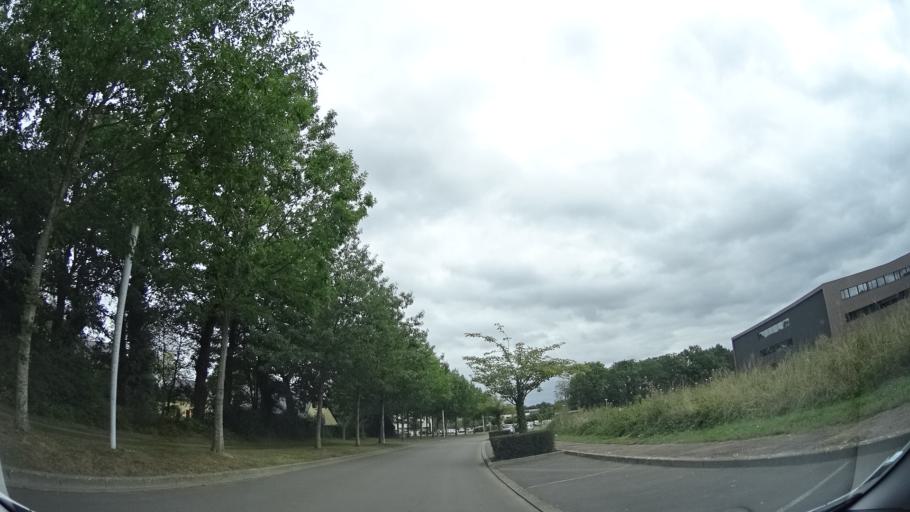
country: FR
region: Brittany
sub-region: Departement d'Ille-et-Vilaine
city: Bruz
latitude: 48.0485
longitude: -1.7460
